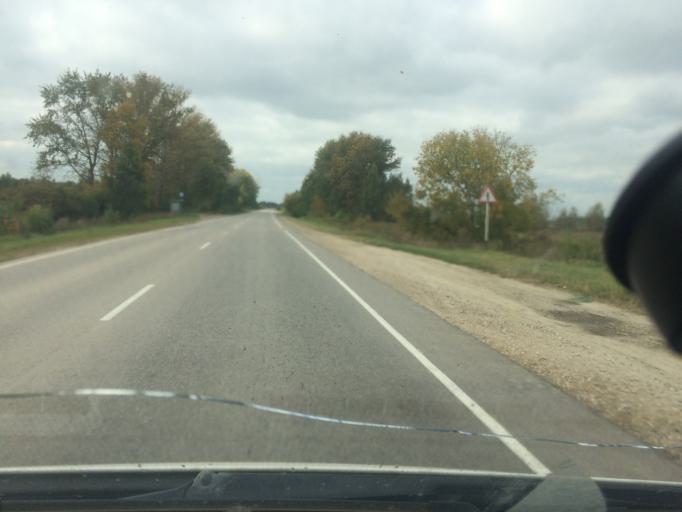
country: RU
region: Tula
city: Odoyev
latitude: 53.9900
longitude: 36.7050
